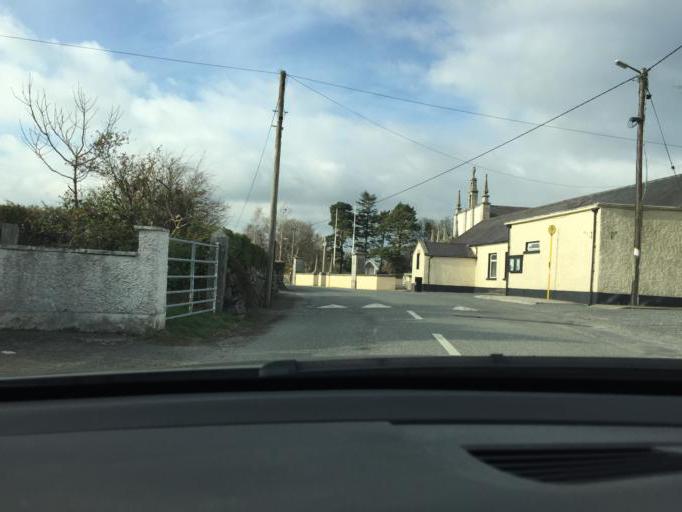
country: IE
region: Leinster
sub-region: Wicklow
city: Valleymount
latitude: 53.1064
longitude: -6.5250
